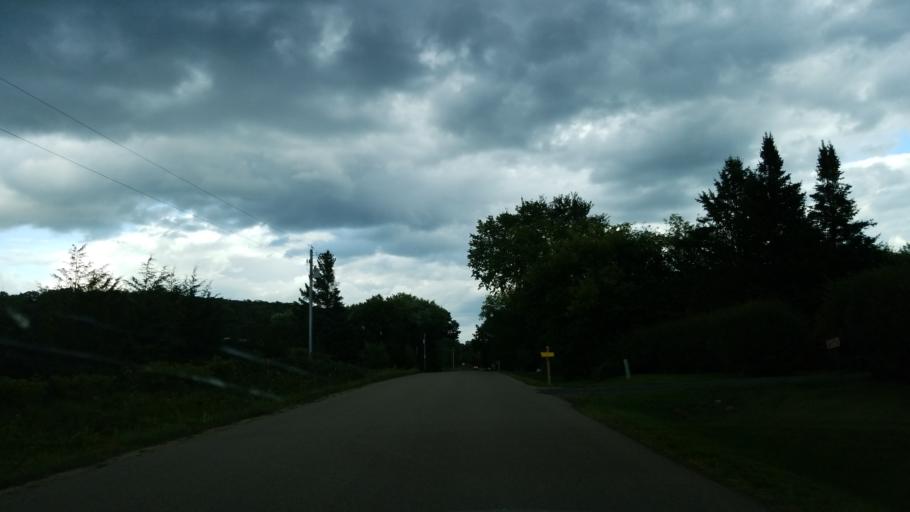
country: US
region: Minnesota
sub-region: Washington County
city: Lake Saint Croix Beach
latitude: 44.8802
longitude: -92.7352
